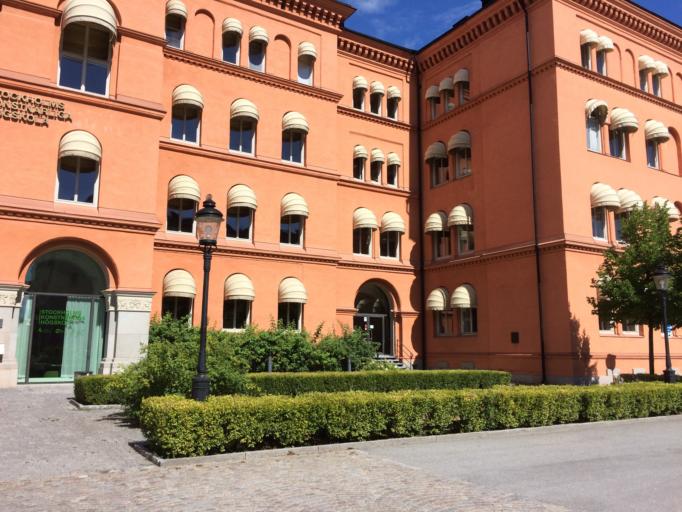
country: SE
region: Stockholm
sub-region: Stockholms Kommun
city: OEstermalm
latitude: 59.3345
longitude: 18.0950
